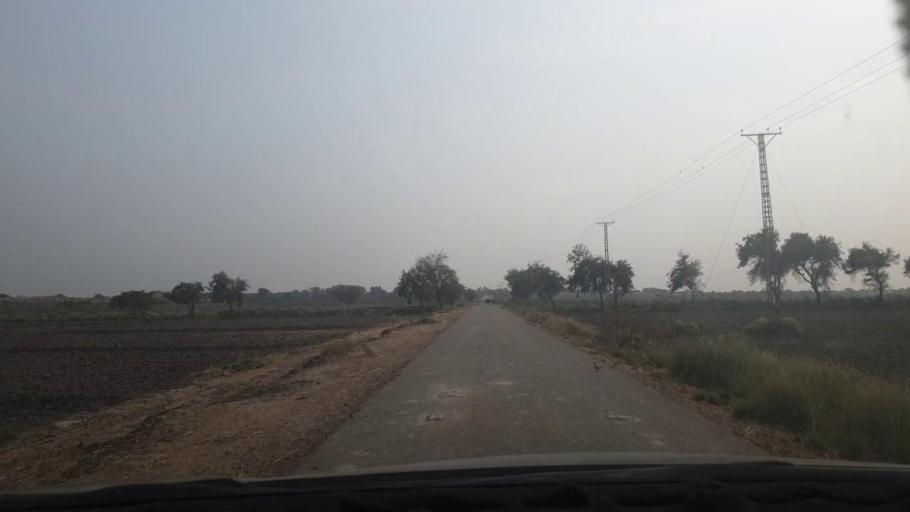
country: PK
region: Sindh
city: Jamshoro
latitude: 25.5117
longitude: 68.3145
